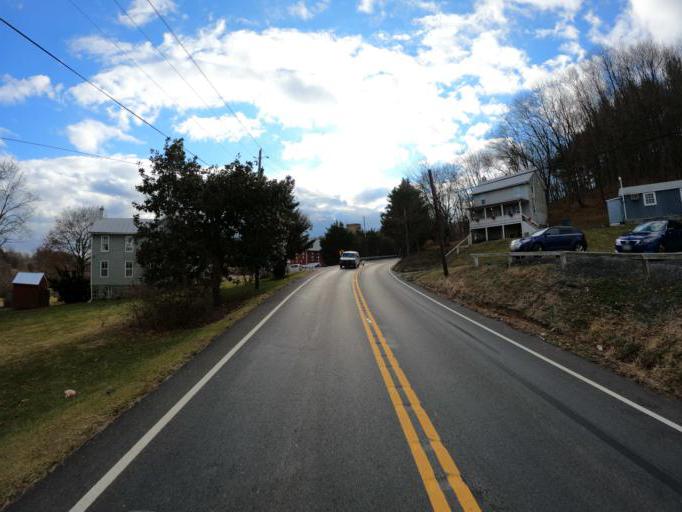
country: US
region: Maryland
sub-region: Carroll County
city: New Windsor
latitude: 39.5063
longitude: -77.1321
